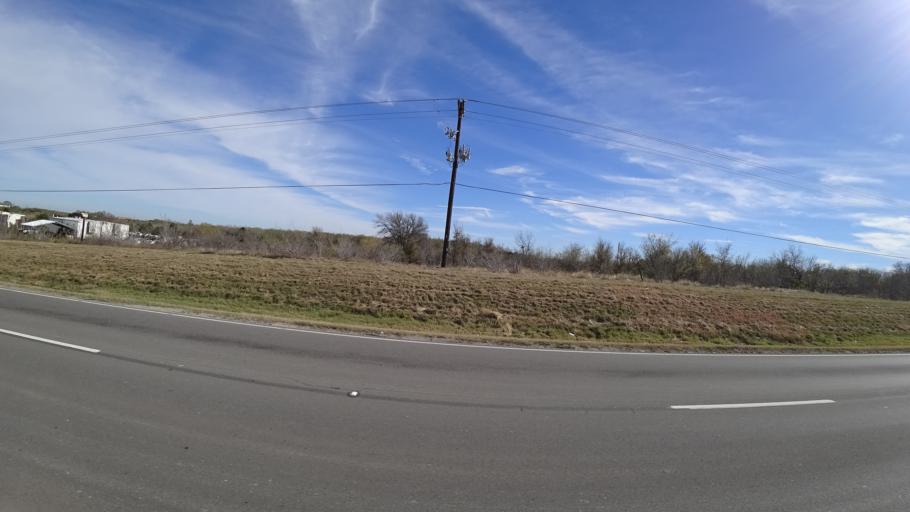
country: US
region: Texas
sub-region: Travis County
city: Onion Creek
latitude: 30.1205
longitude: -97.6954
